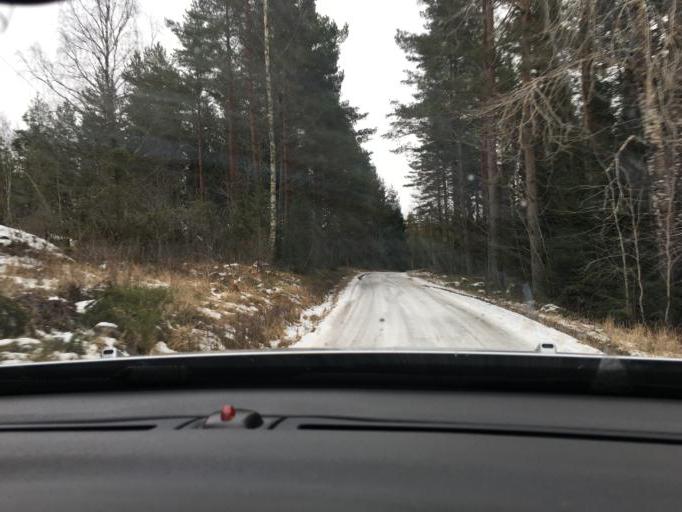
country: SE
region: Soedermanland
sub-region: Katrineholms Kommun
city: Katrineholm
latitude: 58.9992
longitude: 16.2994
